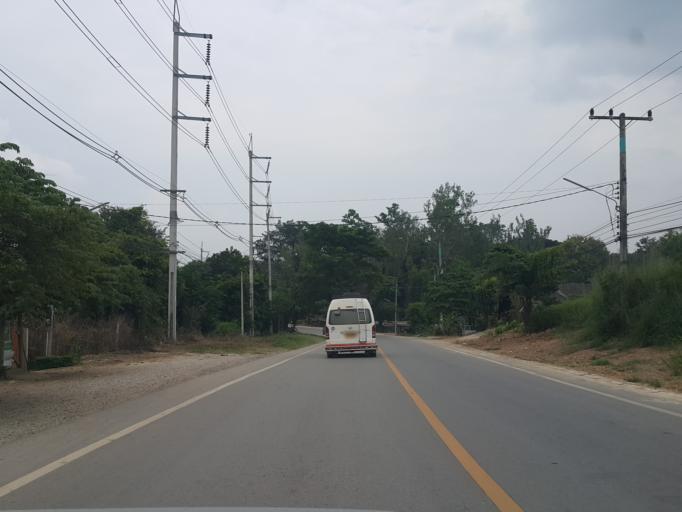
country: TH
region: Chiang Mai
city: Mae Taeng
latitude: 19.0895
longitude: 98.8888
